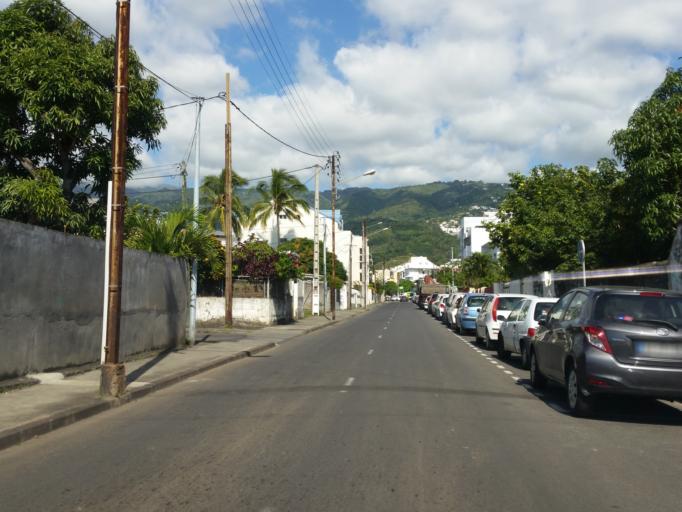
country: RE
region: Reunion
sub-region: Reunion
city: Saint-Denis
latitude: -20.8852
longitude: 55.4594
